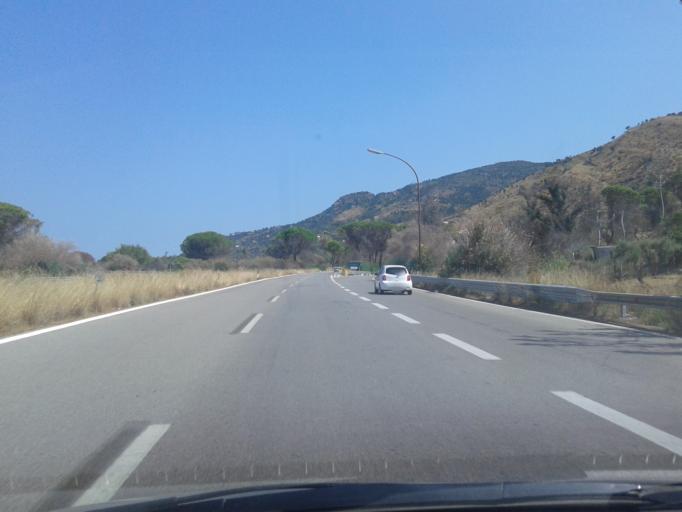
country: IT
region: Sicily
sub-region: Palermo
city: Lascari
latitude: 38.0254
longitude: 13.9667
